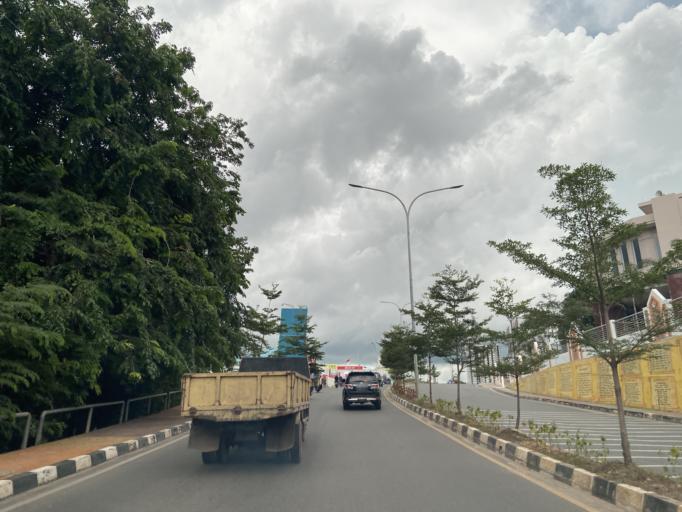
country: SG
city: Singapore
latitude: 1.1462
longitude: 104.0171
